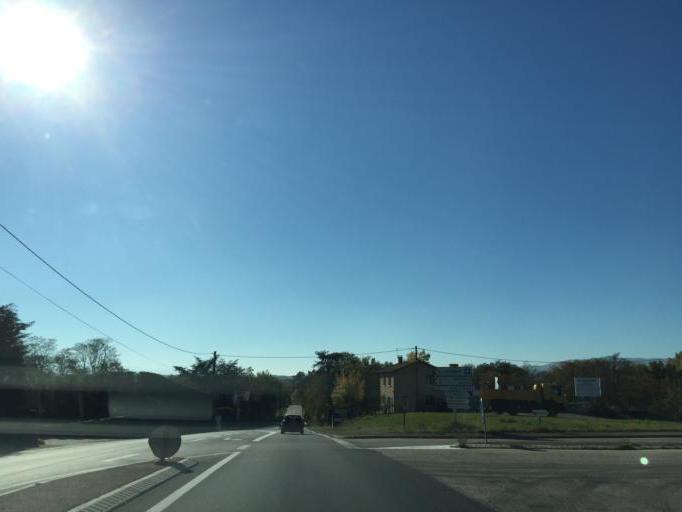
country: FR
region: Rhone-Alpes
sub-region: Departement du Rhone
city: Saint-Andeol-le-Chateau
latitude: 45.6147
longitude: 4.7041
